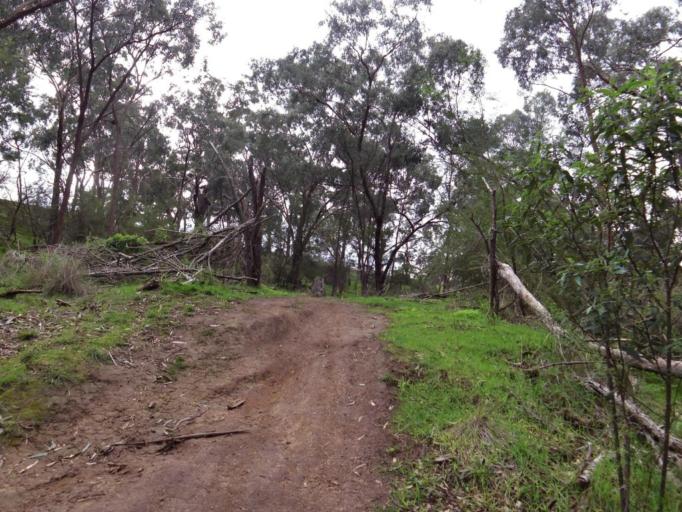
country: AU
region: Victoria
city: Plenty
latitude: -37.6735
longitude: 145.0977
